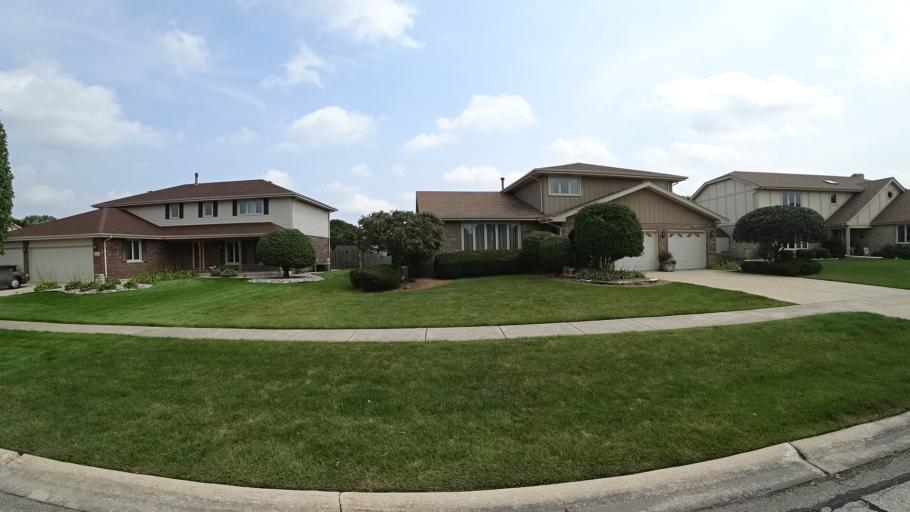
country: US
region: Illinois
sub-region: Will County
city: Goodings Grove
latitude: 41.6205
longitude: -87.9083
